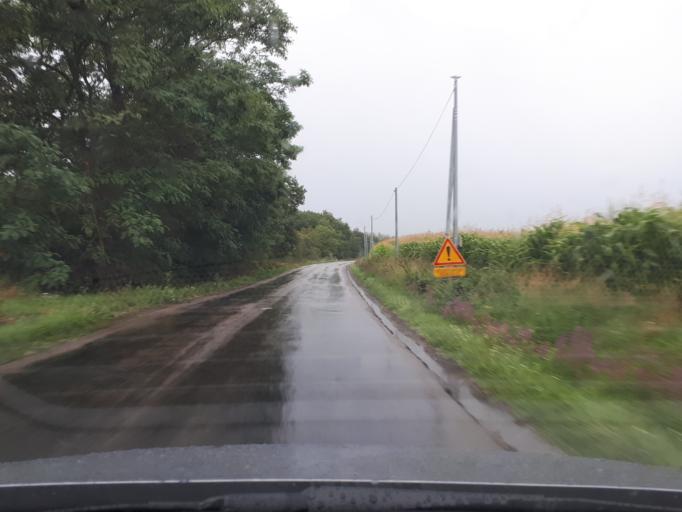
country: FR
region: Rhone-Alpes
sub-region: Departement de la Loire
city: Feurs
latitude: 45.7303
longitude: 4.2391
